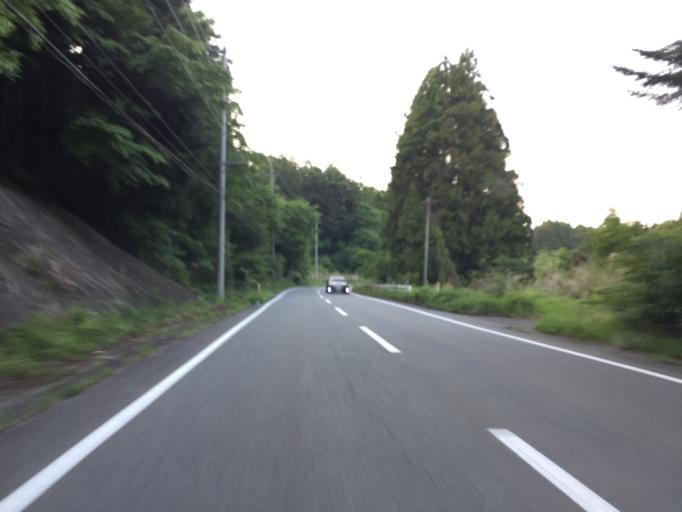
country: JP
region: Fukushima
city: Namie
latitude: 37.2652
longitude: 140.9739
